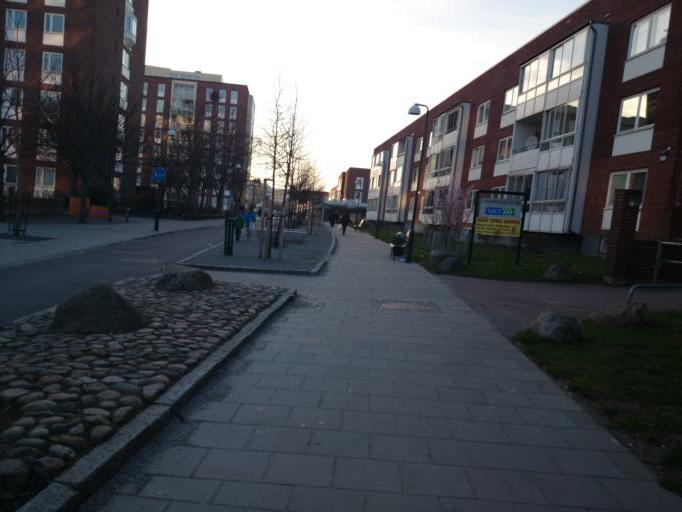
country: SE
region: Skane
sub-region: Malmo
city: Malmoe
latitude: 55.5861
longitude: 13.0405
